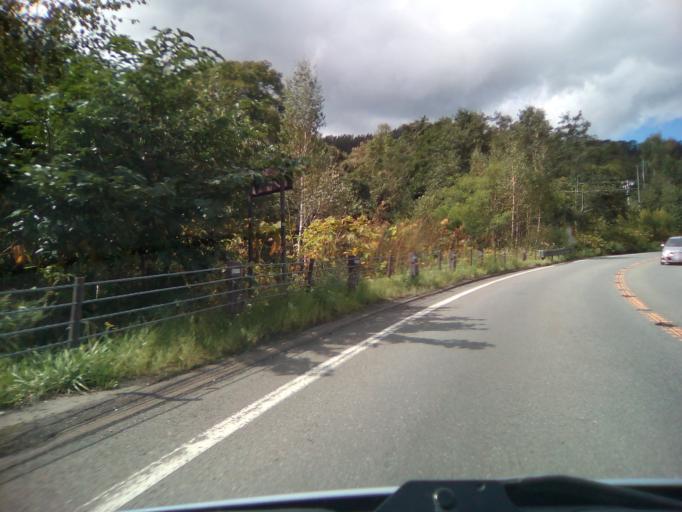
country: JP
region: Hokkaido
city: Date
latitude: 42.5912
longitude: 140.7829
